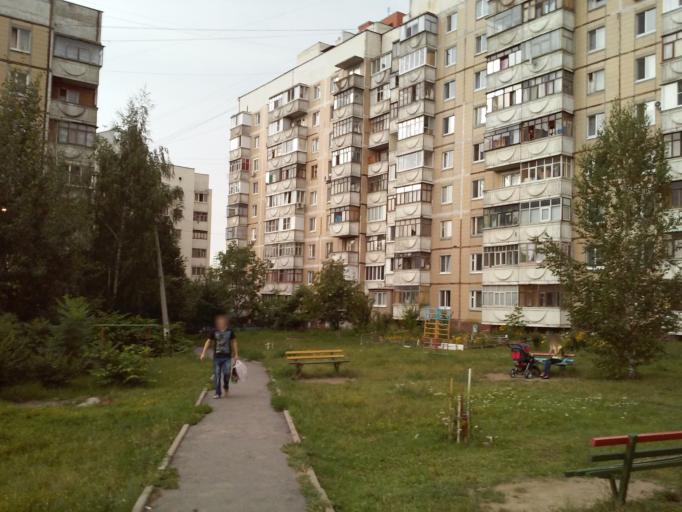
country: RU
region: Belgorod
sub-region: Belgorodskiy Rayon
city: Belgorod
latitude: 50.5682
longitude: 36.5758
